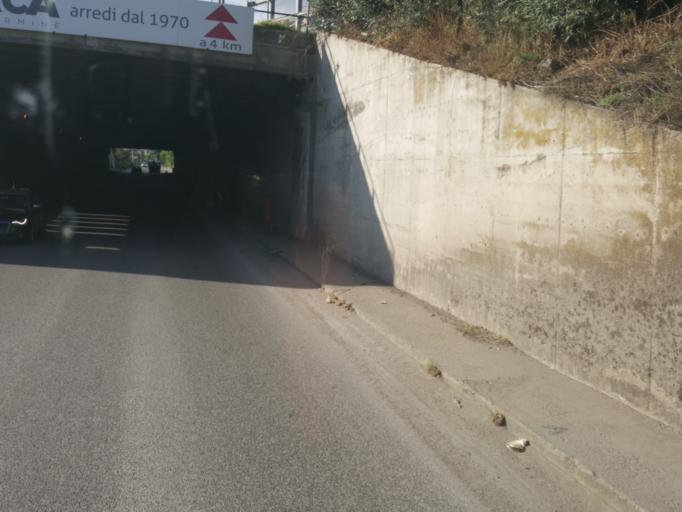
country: IT
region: Campania
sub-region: Provincia di Napoli
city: Nola
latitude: 40.9121
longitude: 14.5273
